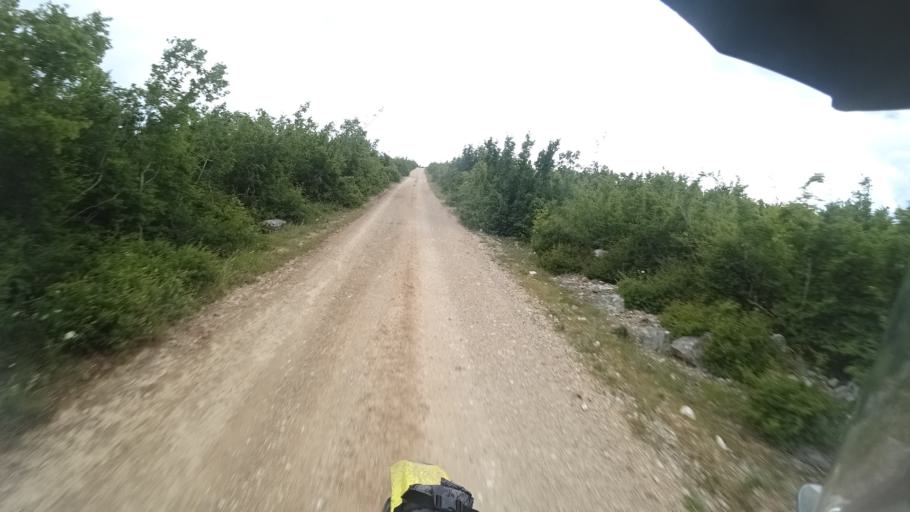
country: HR
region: Sibensko-Kniniska
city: Kistanje
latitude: 44.0994
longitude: 15.9772
